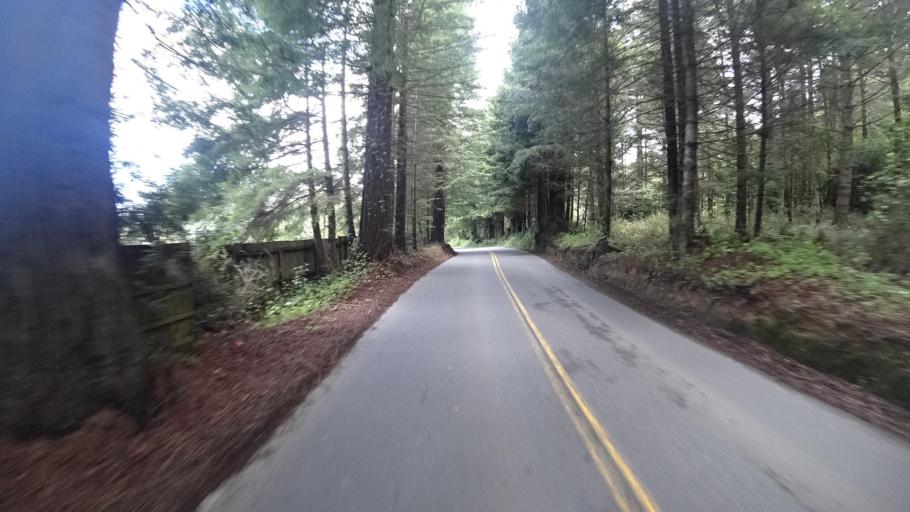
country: US
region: California
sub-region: Humboldt County
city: Blue Lake
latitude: 40.8804
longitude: -123.9785
